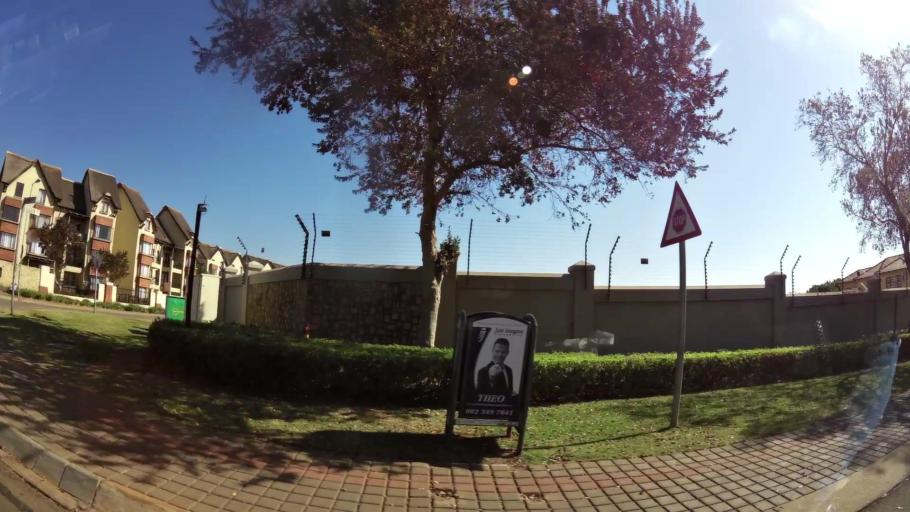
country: ZA
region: Gauteng
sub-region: City of Tshwane Metropolitan Municipality
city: Pretoria
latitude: -25.6796
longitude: 28.2653
